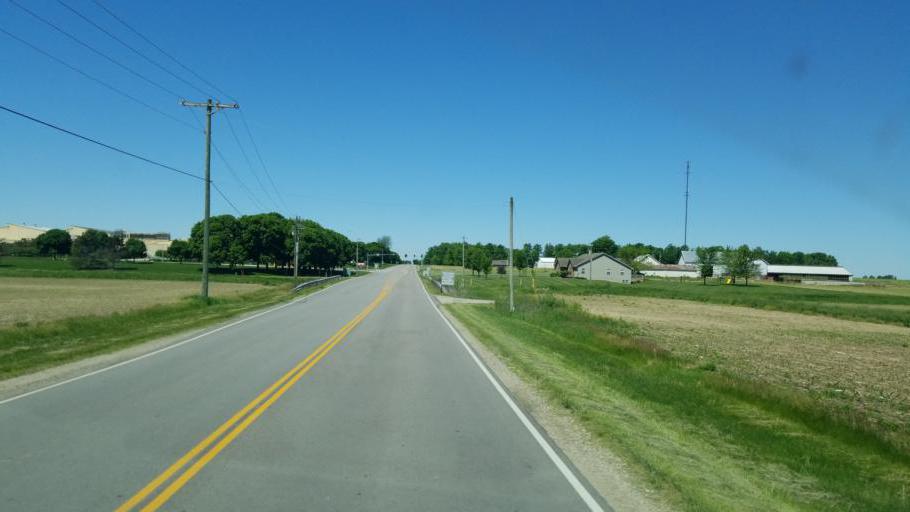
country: US
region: Ohio
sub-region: Shelby County
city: Anna
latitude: 40.3805
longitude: -84.1838
